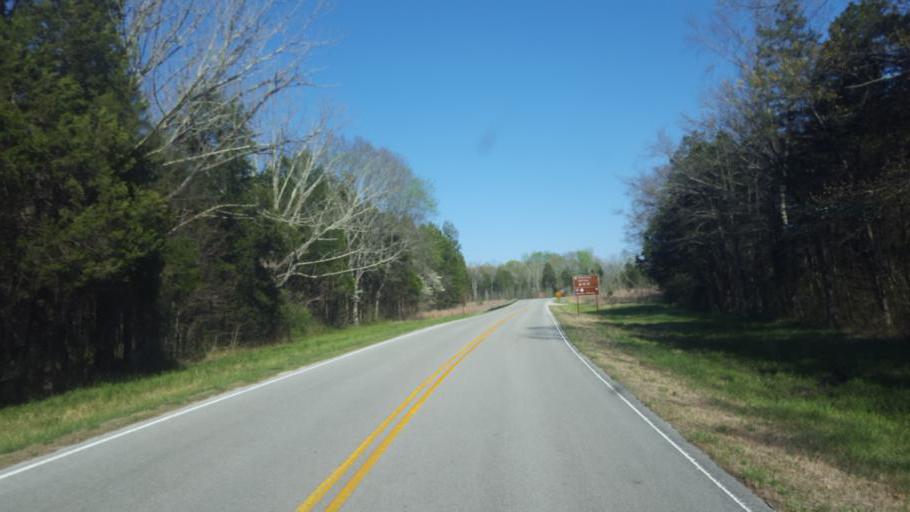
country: US
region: Kentucky
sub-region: Barren County
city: Cave City
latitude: 37.1532
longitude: -86.1026
